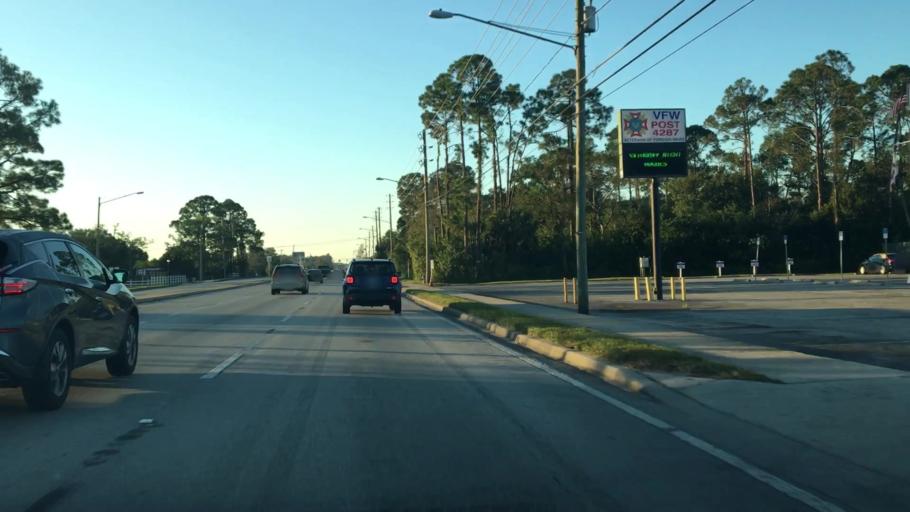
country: US
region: Florida
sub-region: Orange County
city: Conway
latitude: 28.4969
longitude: -81.2855
